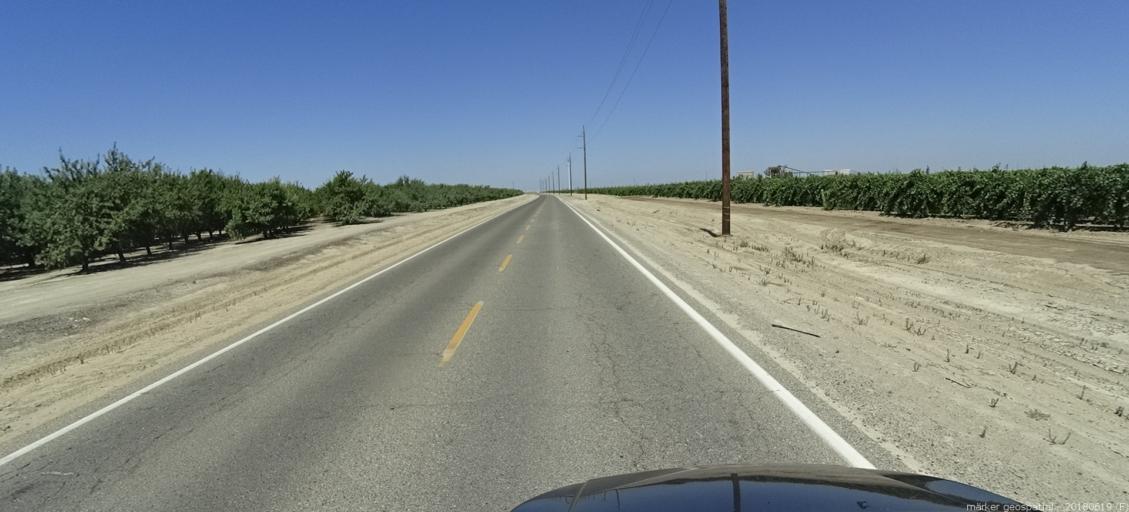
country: US
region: California
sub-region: Fresno County
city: Mendota
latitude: 36.8559
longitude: -120.3314
